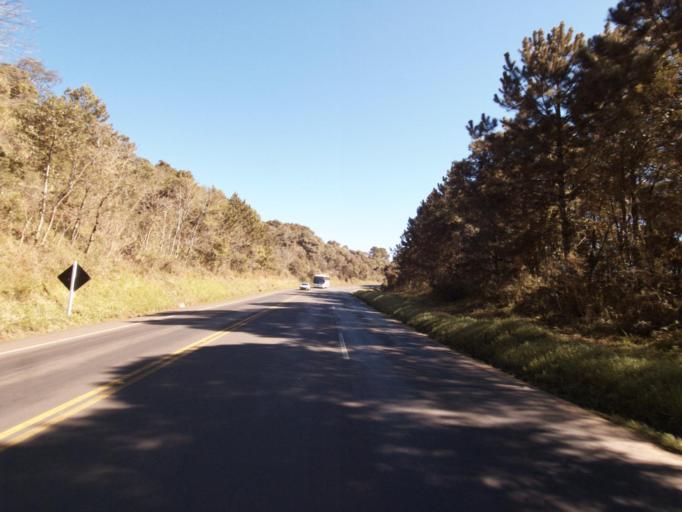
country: BR
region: Santa Catarina
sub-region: Joacaba
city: Joacaba
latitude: -27.1583
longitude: -51.5879
